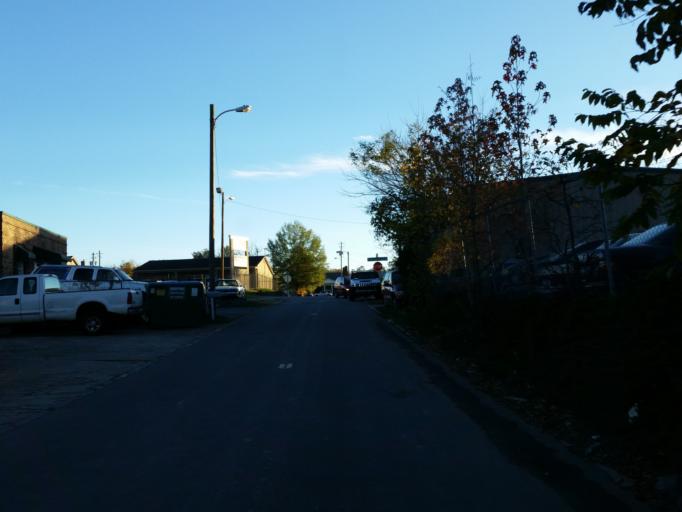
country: US
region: Georgia
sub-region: Cobb County
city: Marietta
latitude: 33.9527
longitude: -84.5347
